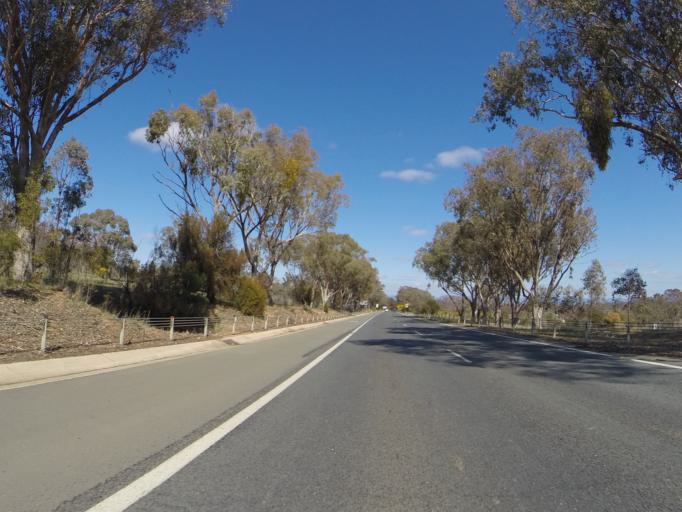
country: AU
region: Australian Capital Territory
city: Kaleen
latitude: -35.2208
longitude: 149.1772
